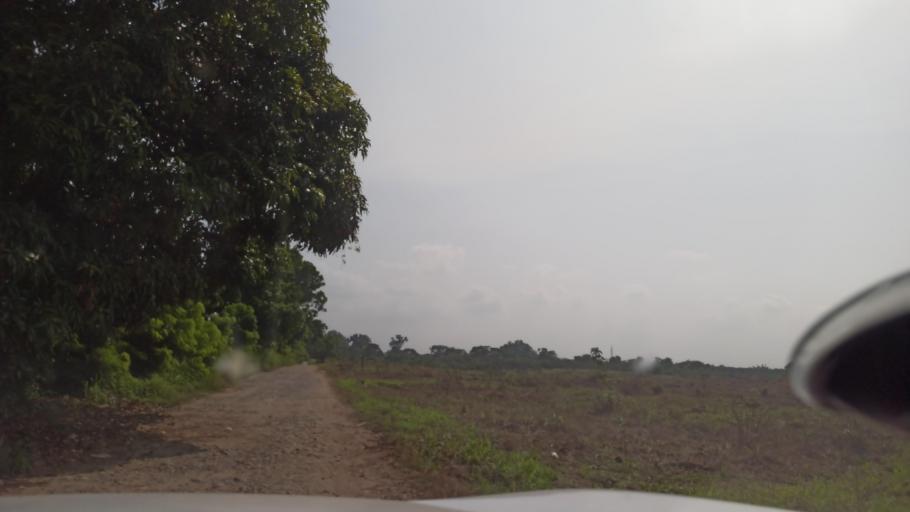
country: MX
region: Veracruz
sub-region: Martinez de la Torre
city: El Progreso
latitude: 20.1466
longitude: -97.0624
